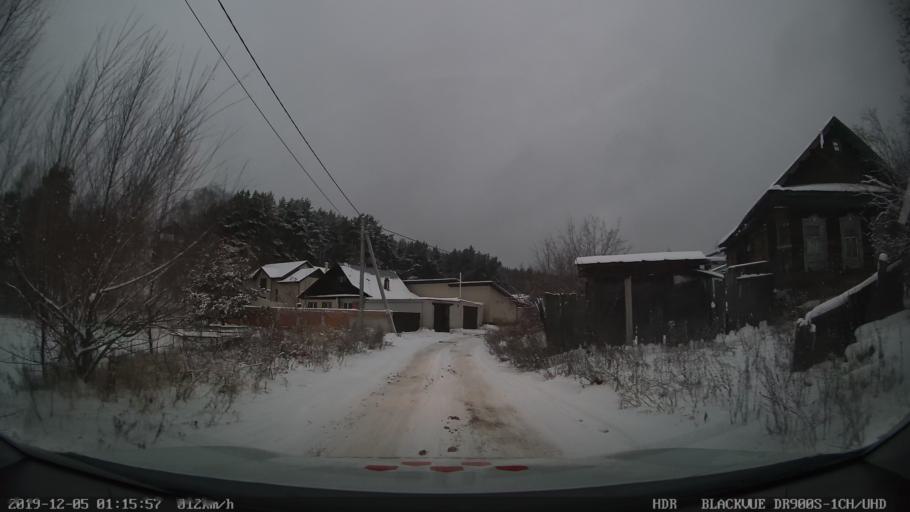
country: RU
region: Tatarstan
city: Stolbishchi
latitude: 55.6461
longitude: 49.1110
